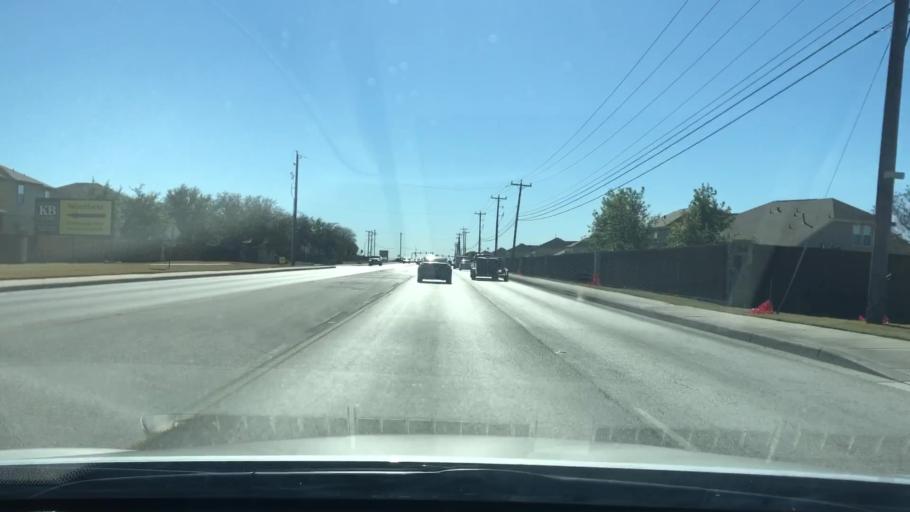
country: US
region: Texas
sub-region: Bexar County
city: Kirby
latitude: 29.4621
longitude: -98.3595
